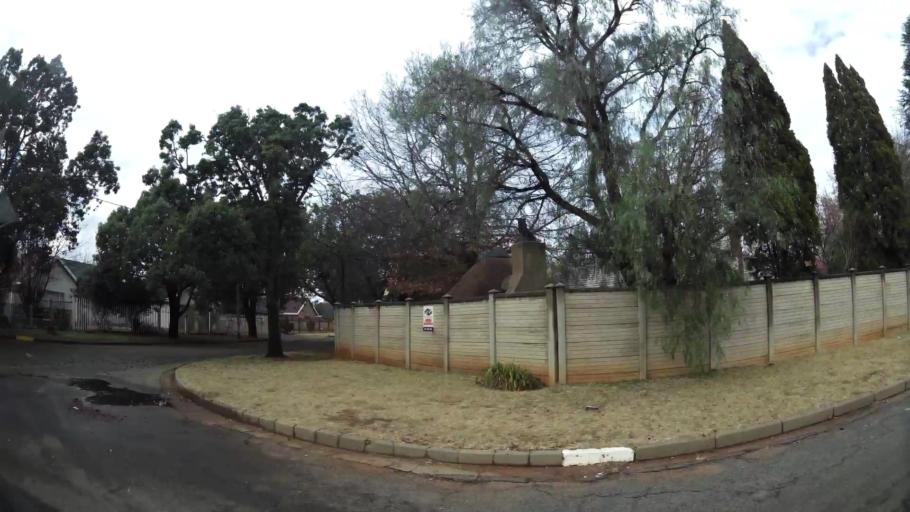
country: ZA
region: Gauteng
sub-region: Sedibeng District Municipality
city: Vereeniging
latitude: -26.6417
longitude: 27.9789
